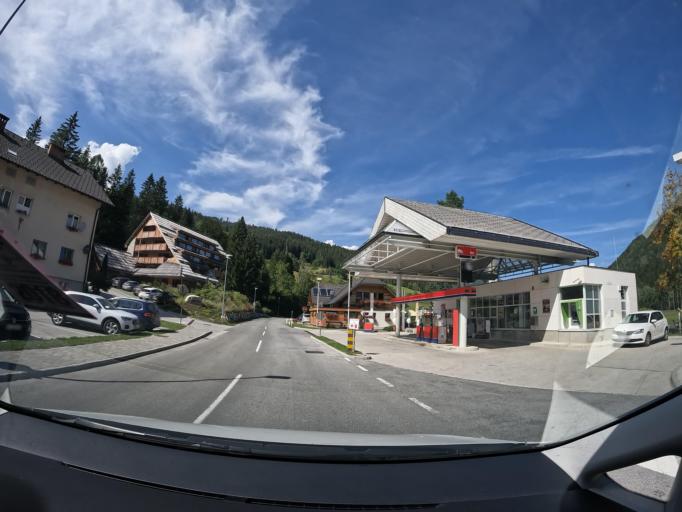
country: AT
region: Carinthia
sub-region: Politischer Bezirk Feldkirchen
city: Feldkirchen in Karnten
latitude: 46.6792
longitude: 14.1247
